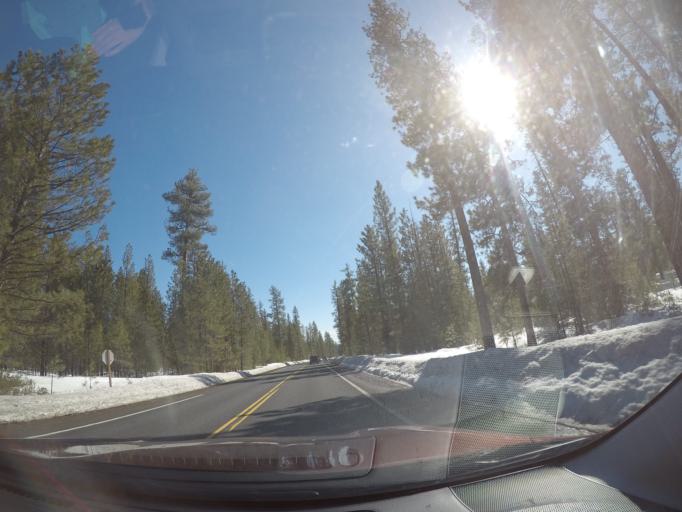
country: US
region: Oregon
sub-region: Deschutes County
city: Three Rivers
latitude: 43.8978
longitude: -121.5919
